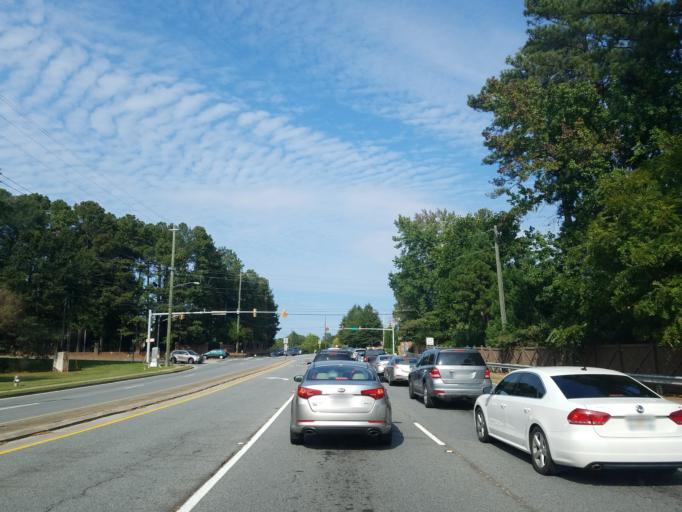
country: US
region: Georgia
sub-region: Fulton County
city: Roswell
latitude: 34.0146
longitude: -84.4307
